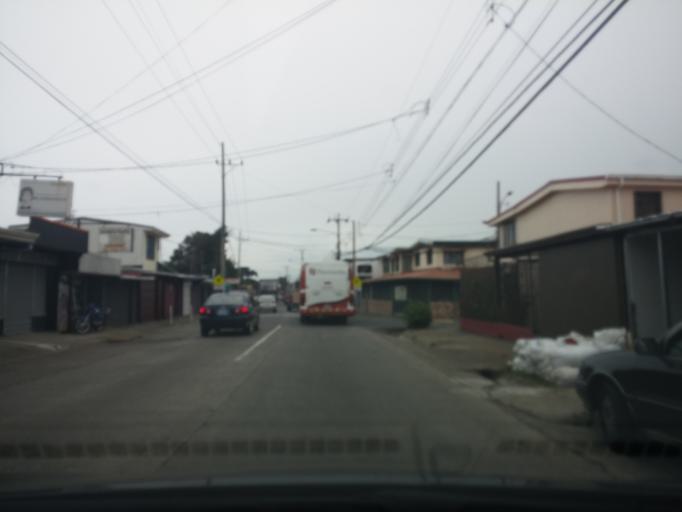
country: CR
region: Heredia
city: Llorente
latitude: 9.9887
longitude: -84.1496
